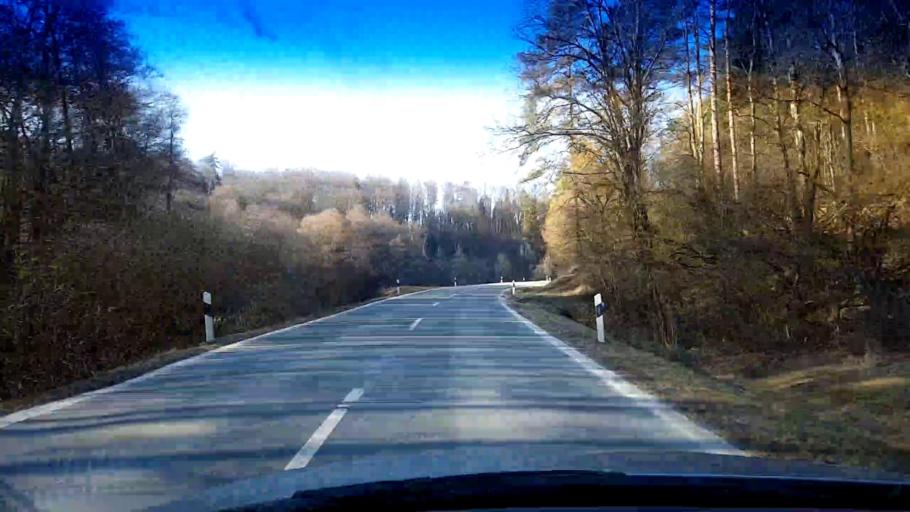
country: DE
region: Bavaria
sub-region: Upper Franconia
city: Aufsess
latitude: 49.8880
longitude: 11.2241
